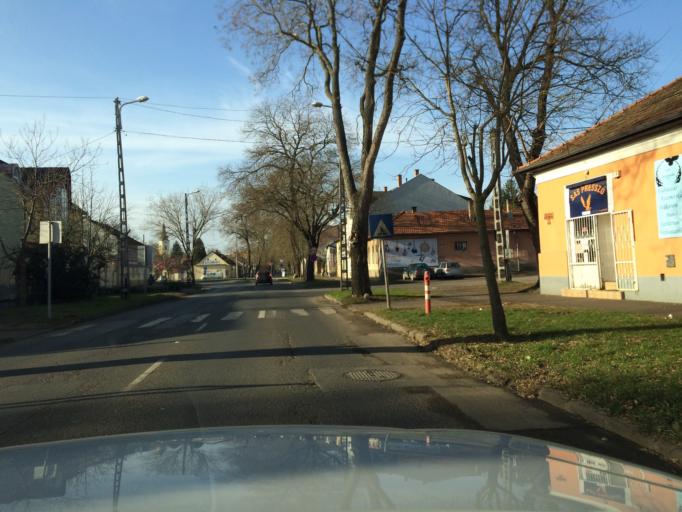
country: HU
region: Szabolcs-Szatmar-Bereg
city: Nyiregyhaza
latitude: 47.9513
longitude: 21.7256
